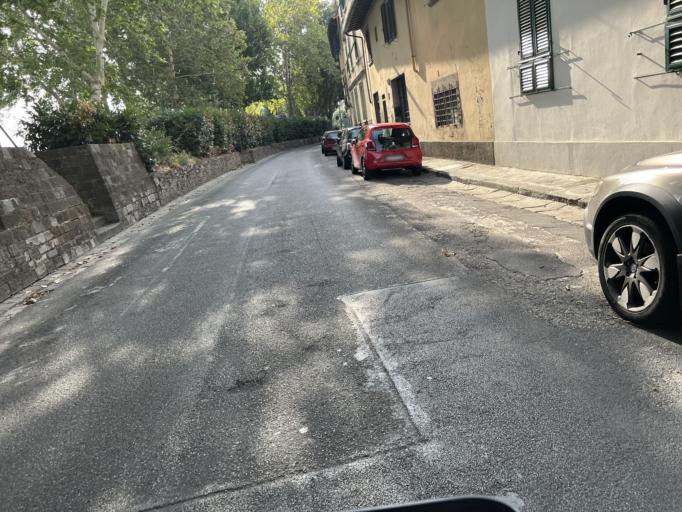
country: IT
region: Tuscany
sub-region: Province of Florence
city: Florence
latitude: 43.7733
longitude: 11.2365
